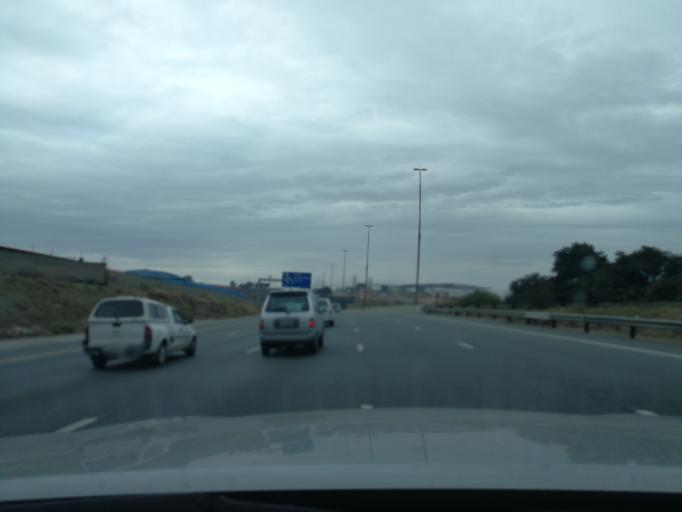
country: ZA
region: Gauteng
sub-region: Ekurhuleni Metropolitan Municipality
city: Germiston
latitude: -26.2416
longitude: 28.1306
